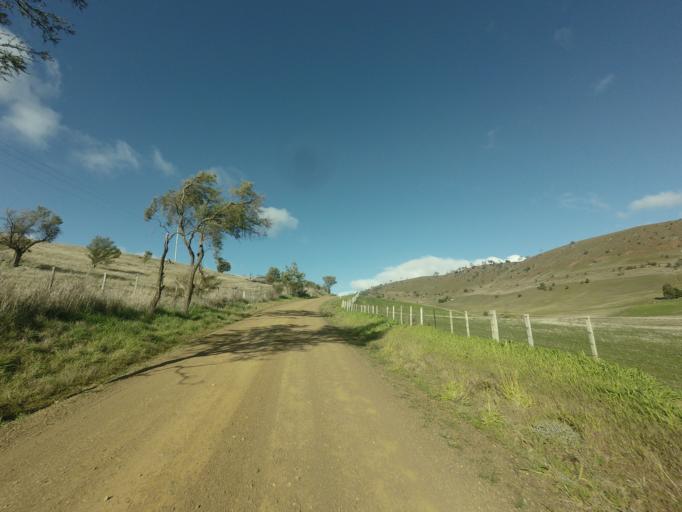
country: AU
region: Tasmania
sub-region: Derwent Valley
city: New Norfolk
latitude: -42.7022
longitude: 146.9896
